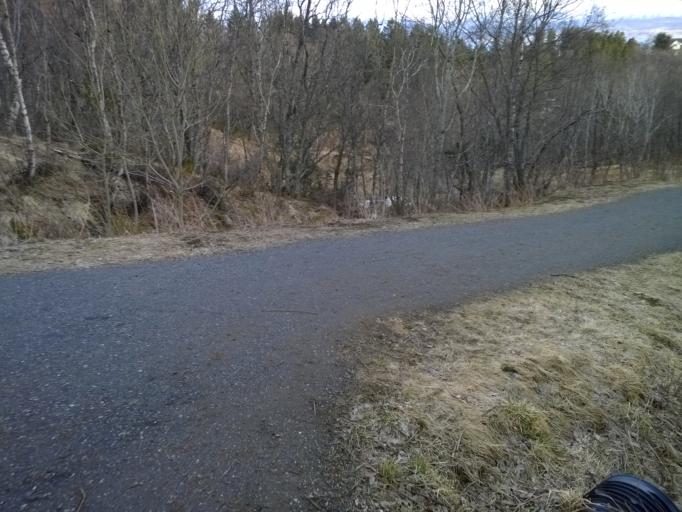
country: NO
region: Nordland
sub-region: Bodo
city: Lopsmarka
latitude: 67.2870
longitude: 14.5205
